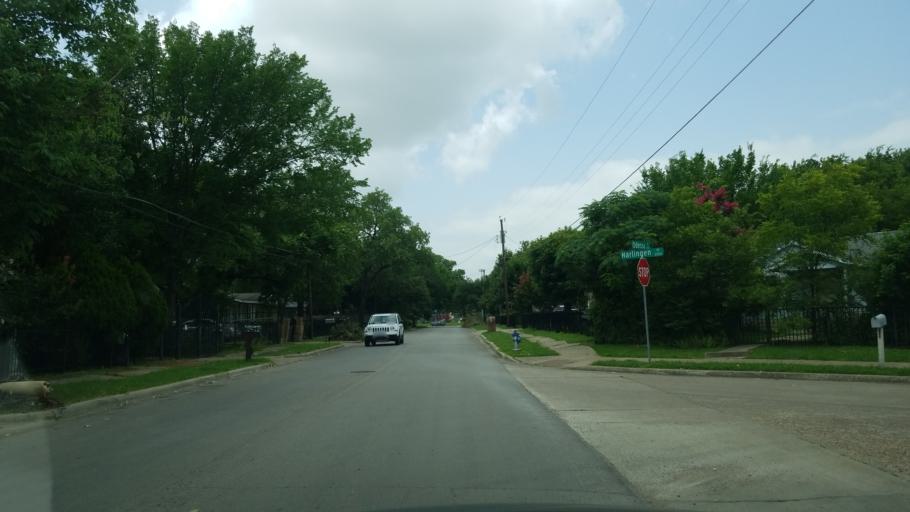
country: US
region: Texas
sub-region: Dallas County
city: Cockrell Hill
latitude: 32.7821
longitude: -96.9045
